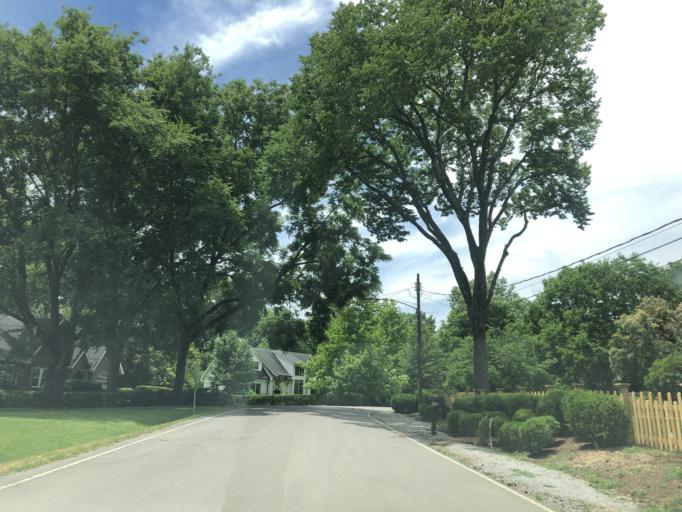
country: US
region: Tennessee
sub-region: Davidson County
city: Oak Hill
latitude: 36.1118
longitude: -86.7938
